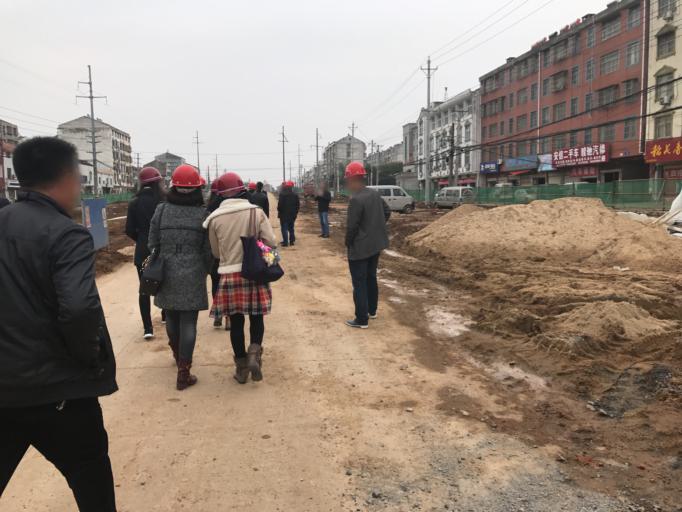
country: CN
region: Hubei
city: Anlu
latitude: 31.2520
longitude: 113.7051
